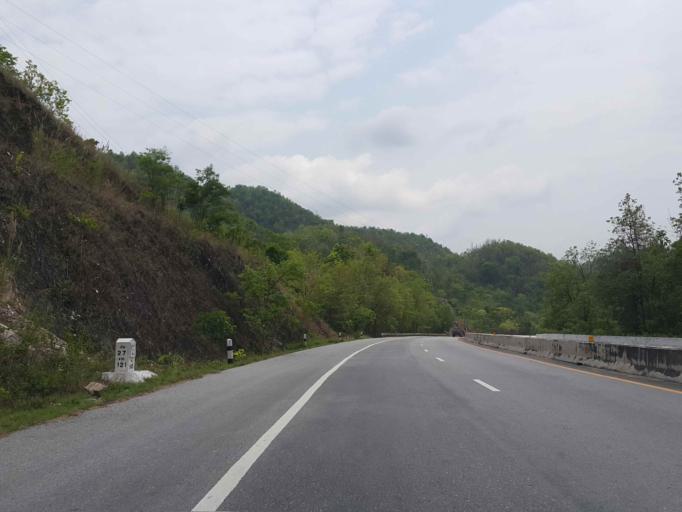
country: TH
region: Lampang
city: Sop Prap
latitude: 17.8423
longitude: 99.2937
